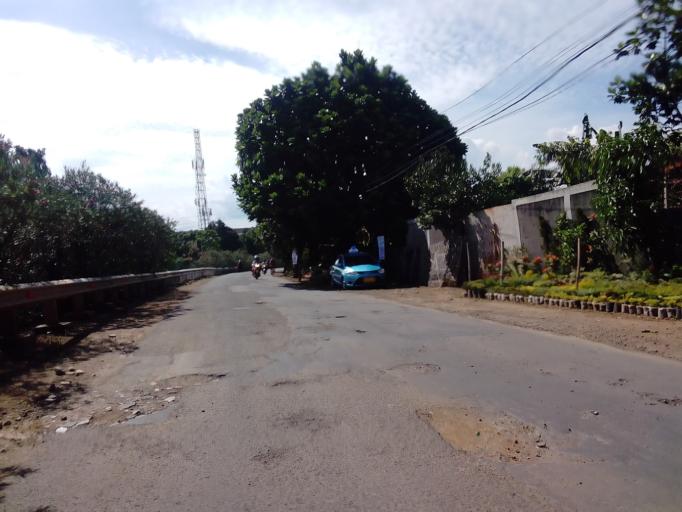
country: ID
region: West Java
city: Bandung
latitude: -6.9434
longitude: 107.6698
